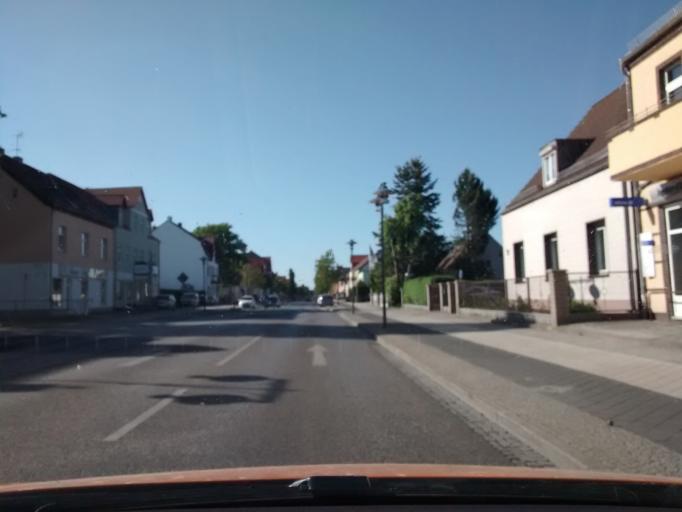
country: DE
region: Brandenburg
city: Furstenwalde
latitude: 52.3441
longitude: 14.0729
